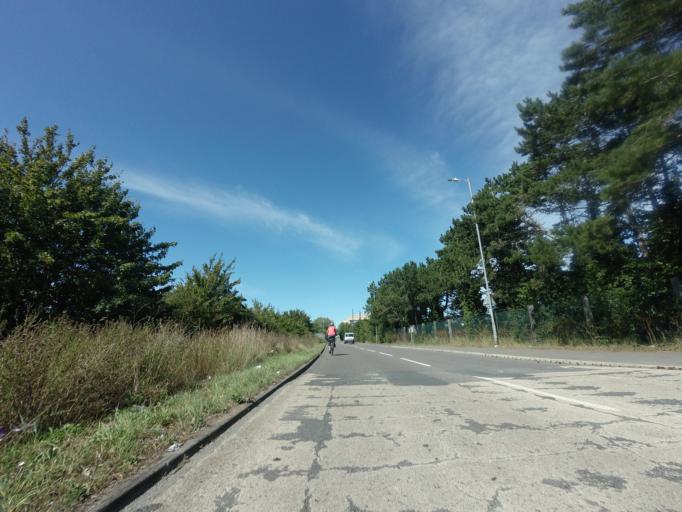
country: GB
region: England
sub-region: Kent
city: Sandwich
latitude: 51.2824
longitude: 1.3452
